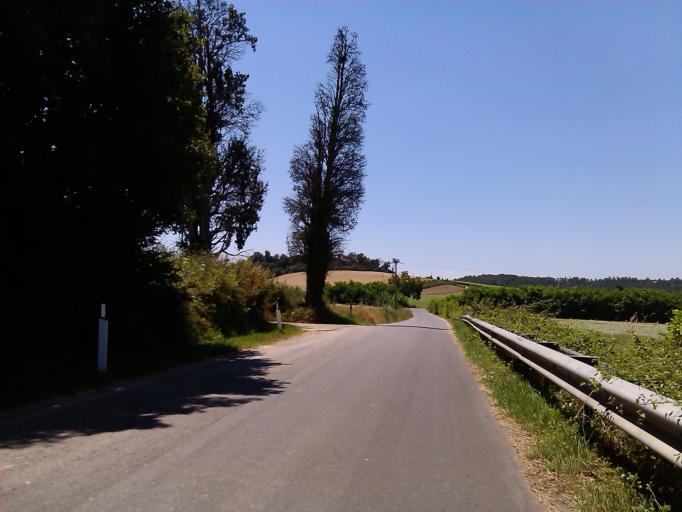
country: IT
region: Umbria
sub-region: Provincia di Terni
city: Fabro Scalo
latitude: 42.8570
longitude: 12.0436
